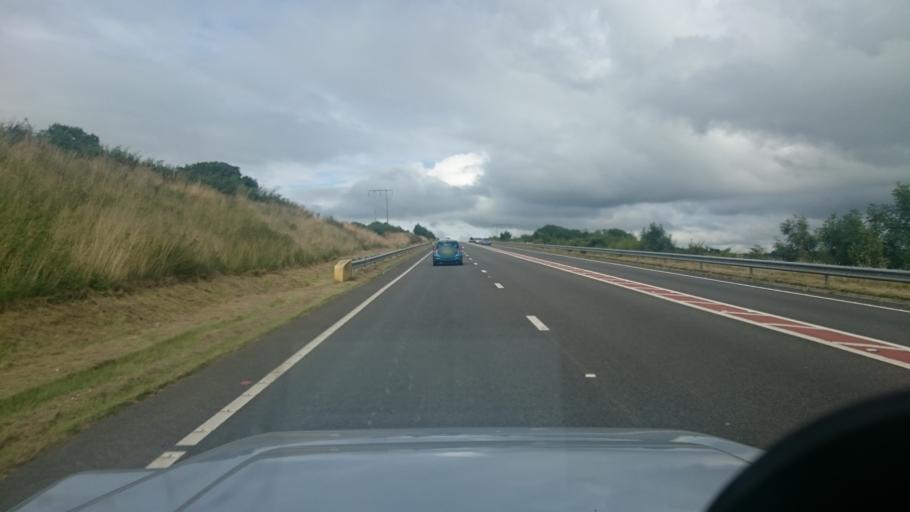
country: GB
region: Wales
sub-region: Pembrokeshire
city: Narberth
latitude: 51.8027
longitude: -4.7895
